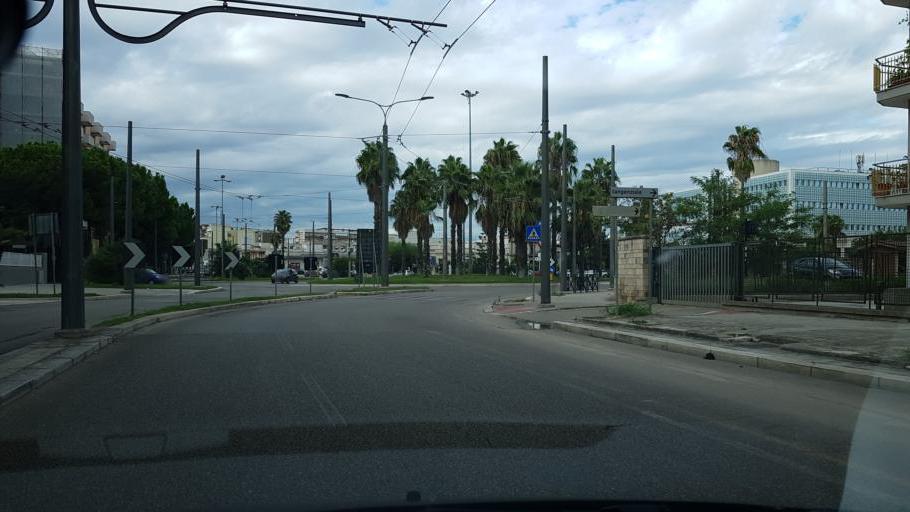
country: IT
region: Apulia
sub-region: Provincia di Lecce
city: Lecce
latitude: 40.3583
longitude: 18.1832
